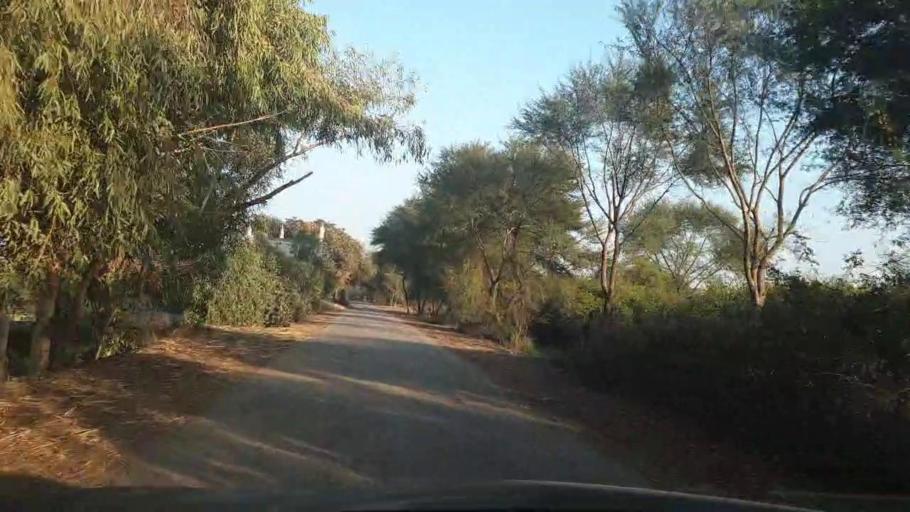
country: PK
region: Sindh
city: Ubauro
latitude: 28.1715
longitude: 69.5848
